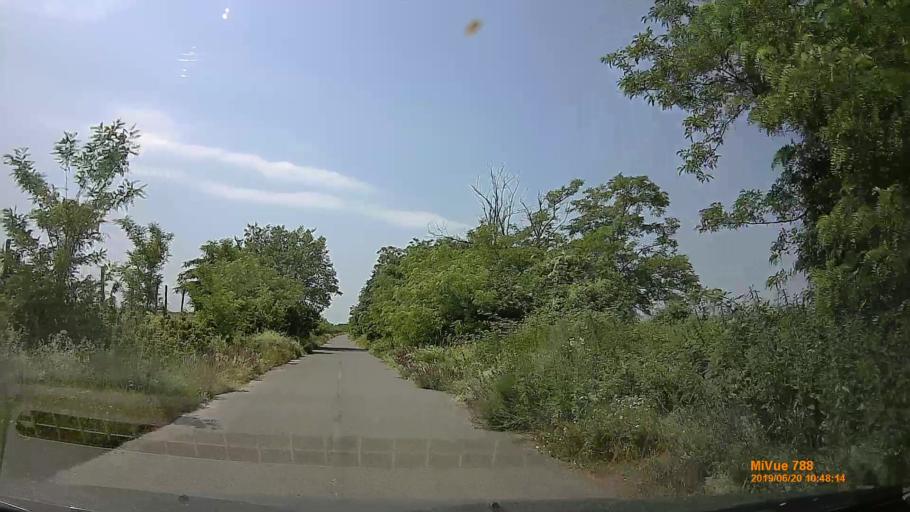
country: HU
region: Baranya
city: Hidas
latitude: 46.1710
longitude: 18.5823
